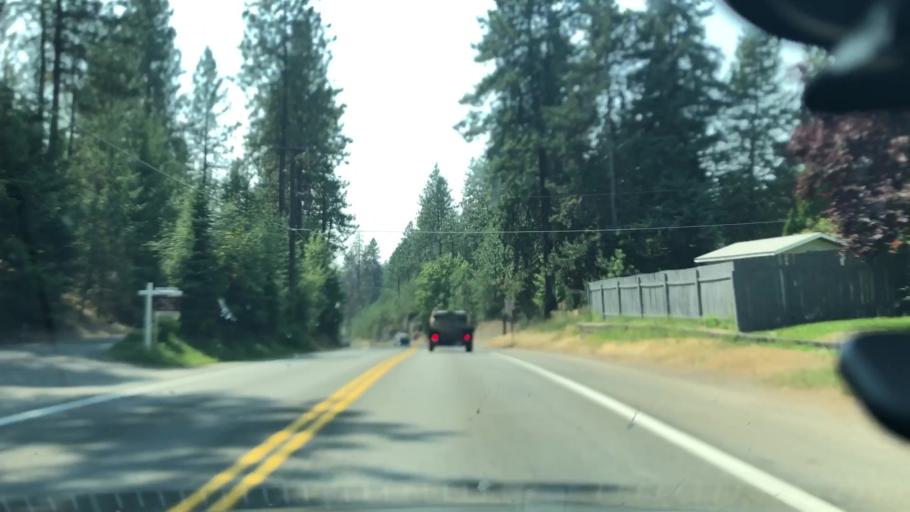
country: US
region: Washington
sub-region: Spokane County
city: Millwood
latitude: 47.6964
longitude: -117.3009
